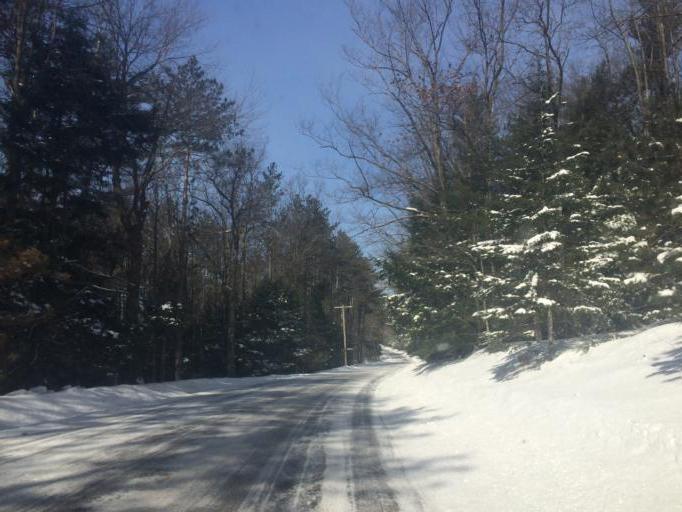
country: US
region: Pennsylvania
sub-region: Centre County
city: Stormstown
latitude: 40.8973
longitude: -78.0460
